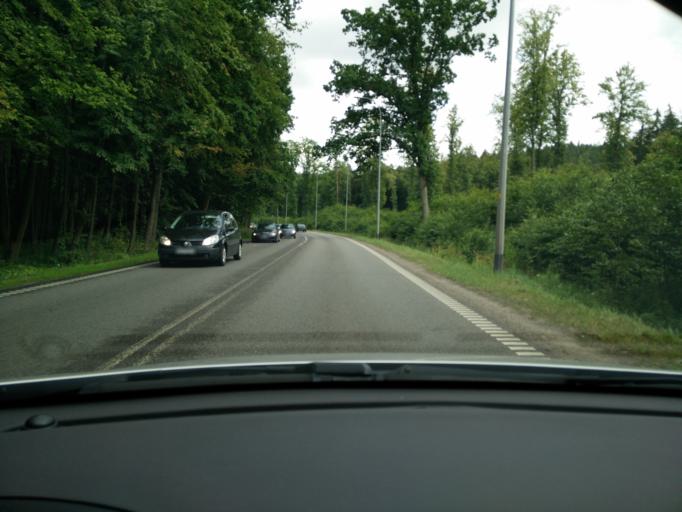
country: PL
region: Pomeranian Voivodeship
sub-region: Gdynia
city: Wielki Kack
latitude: 54.4236
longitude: 18.5048
